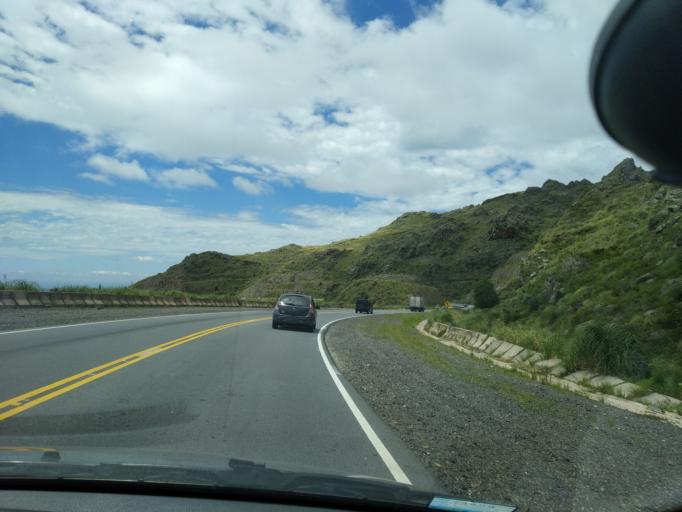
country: AR
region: Cordoba
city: Cuesta Blanca
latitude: -31.6110
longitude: -64.6928
